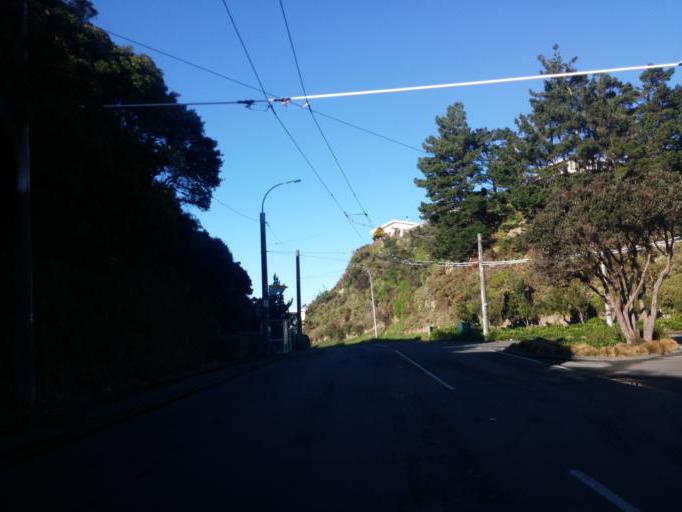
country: NZ
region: Wellington
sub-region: Wellington City
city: Brooklyn
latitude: -41.3234
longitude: 174.7635
